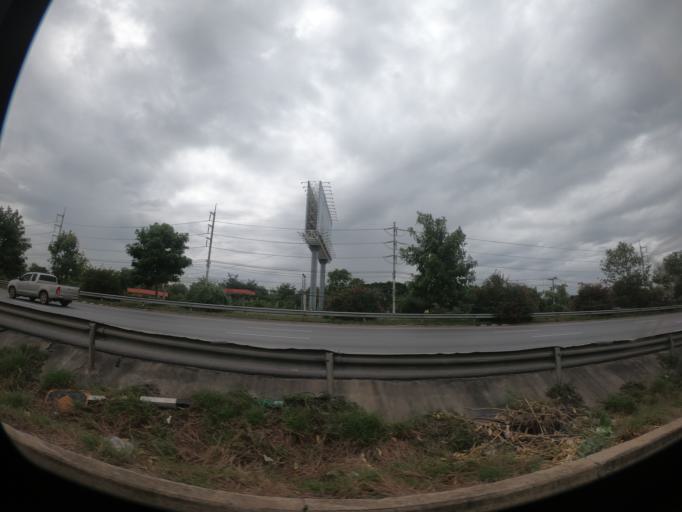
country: TH
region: Sara Buri
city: Nong Khae
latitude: 14.3648
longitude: 100.8776
